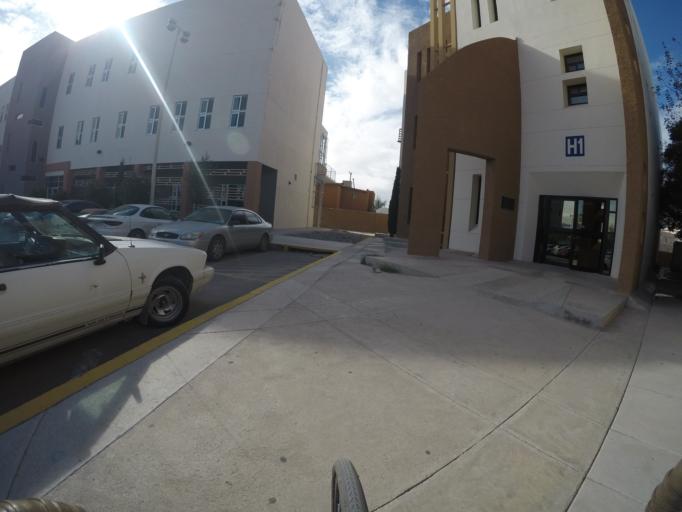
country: MX
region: Chihuahua
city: Ciudad Juarez
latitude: 31.7429
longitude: -106.4305
